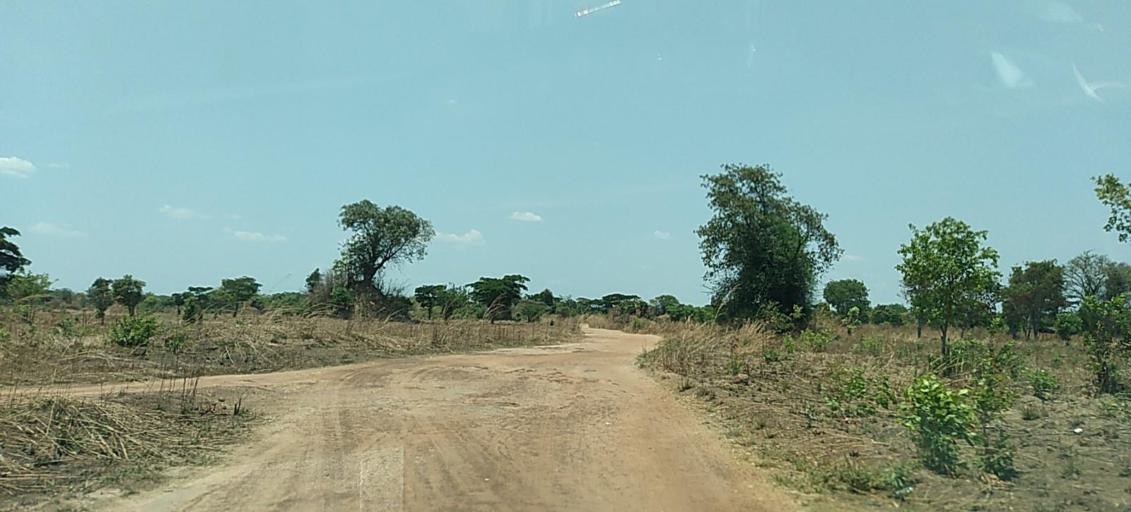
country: ZM
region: Copperbelt
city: Luanshya
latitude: -13.0940
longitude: 28.4066
